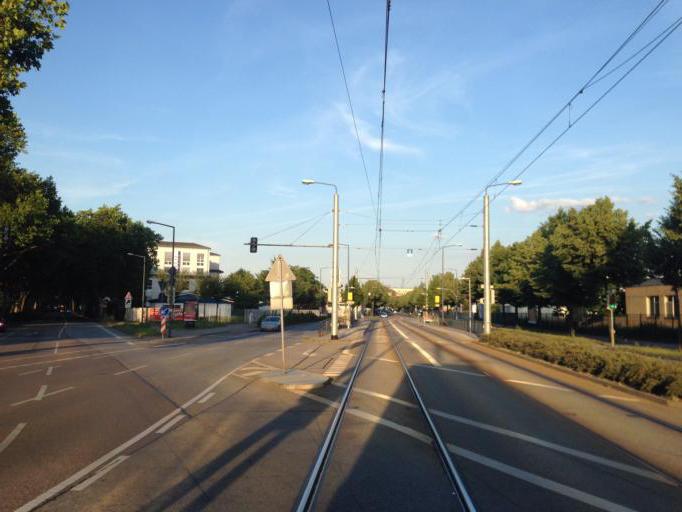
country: DE
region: Saxony
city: Dresden
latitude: 51.0609
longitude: 13.6942
